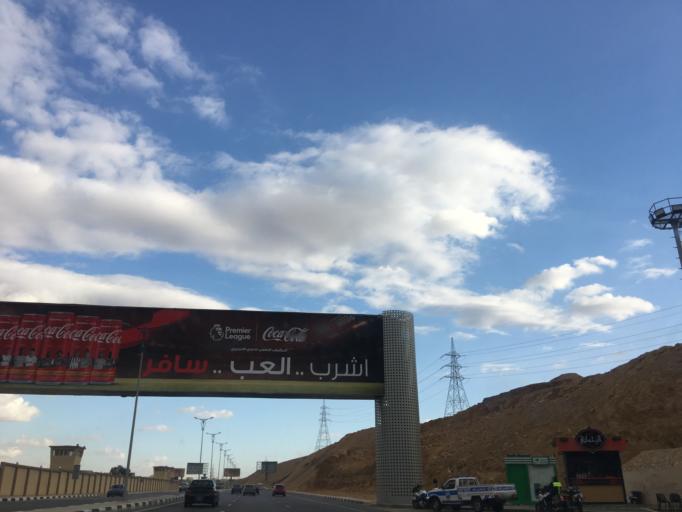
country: EG
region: Muhafazat al Qahirah
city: Cairo
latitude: 30.0212
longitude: 31.3298
